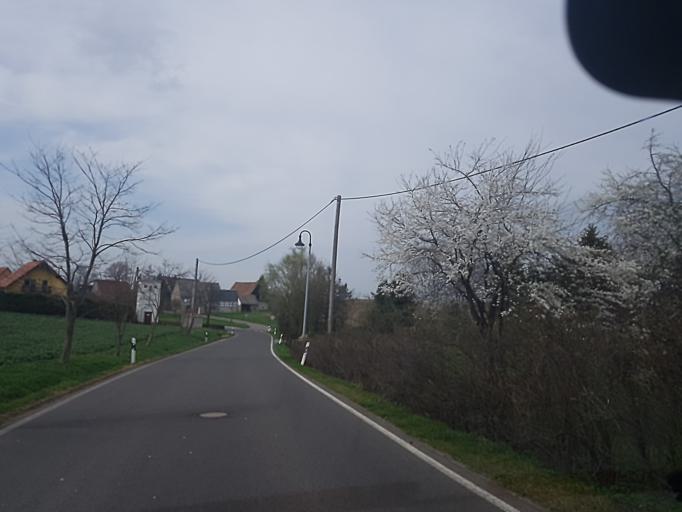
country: DE
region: Saxony
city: Bockelwitz
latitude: 51.2081
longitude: 12.9867
